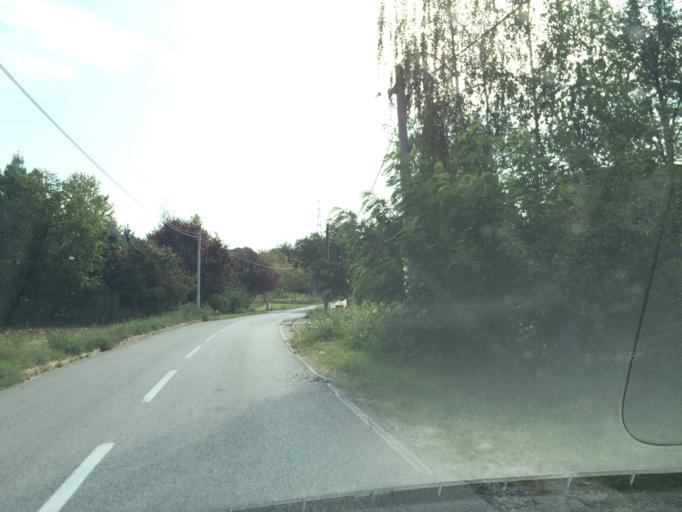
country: RS
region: Autonomna Pokrajina Vojvodina
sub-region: Juznobacki Okrug
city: Novi Sad
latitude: 45.2122
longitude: 19.8351
